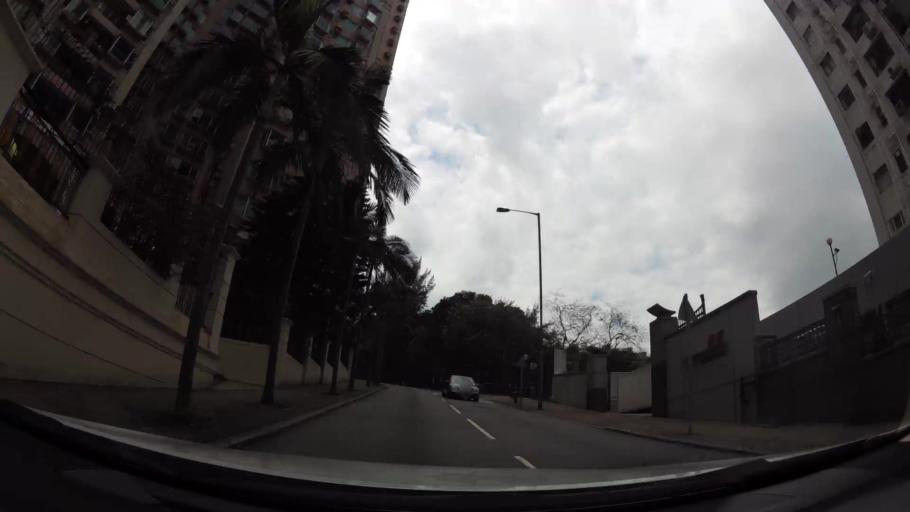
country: HK
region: Wanchai
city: Wan Chai
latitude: 22.2881
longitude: 114.2027
